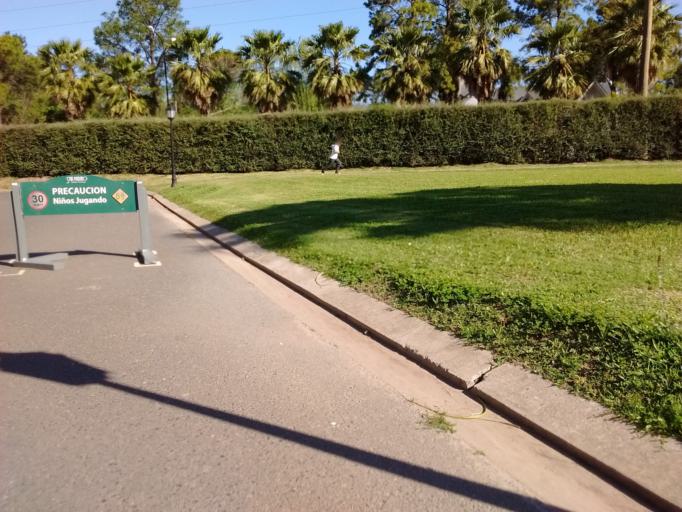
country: AR
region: Santa Fe
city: Funes
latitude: -32.9291
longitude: -60.8223
